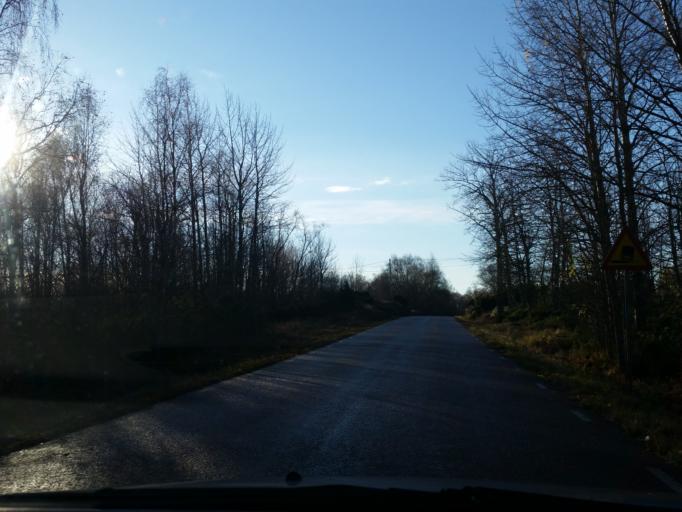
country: AX
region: Alands skaergard
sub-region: Braendoe
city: Braendoe
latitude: 60.4326
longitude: 21.0348
